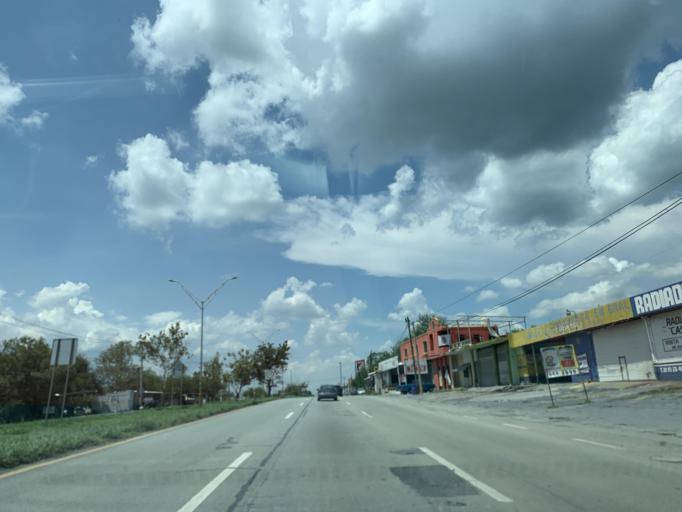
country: MX
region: Nuevo Leon
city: Santiago
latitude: 25.3827
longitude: -100.1139
